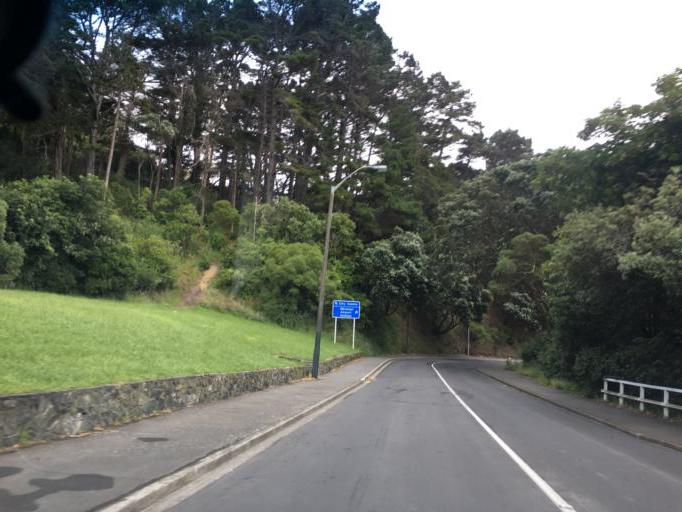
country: NZ
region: Wellington
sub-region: Wellington City
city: Wellington
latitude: -41.3127
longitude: 174.7900
